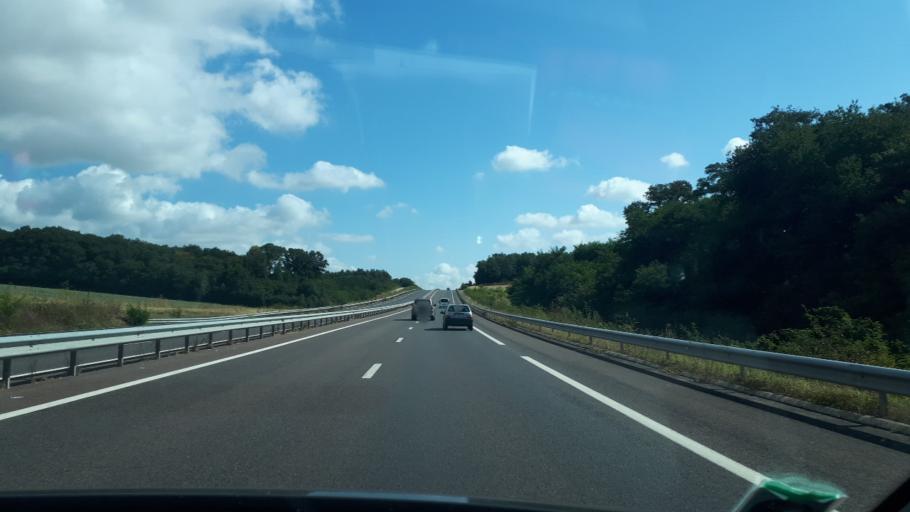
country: FR
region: Centre
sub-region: Departement du Loir-et-Cher
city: Saint-Ouen
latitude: 47.8585
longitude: 1.1122
